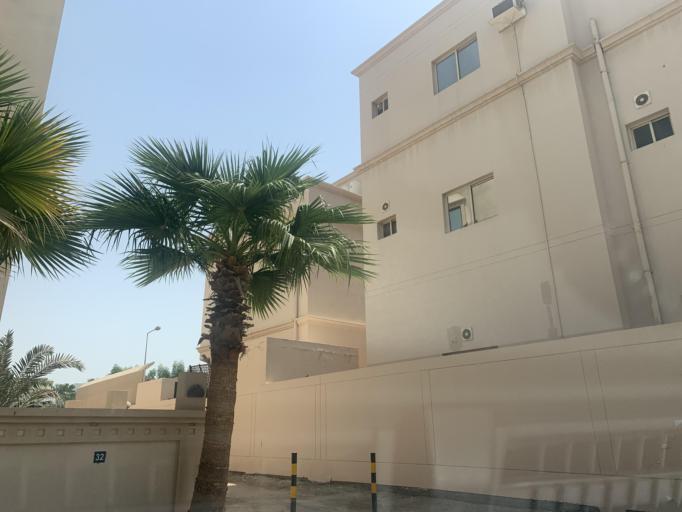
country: BH
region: Manama
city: Jidd Hafs
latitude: 26.1983
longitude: 50.5038
